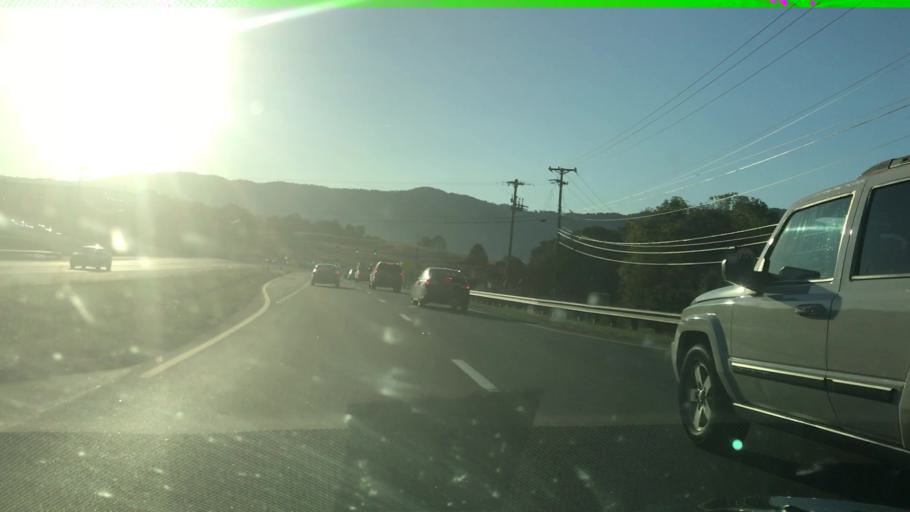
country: US
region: Virginia
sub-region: Botetourt County
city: Laymantown
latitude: 37.3431
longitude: -79.8797
